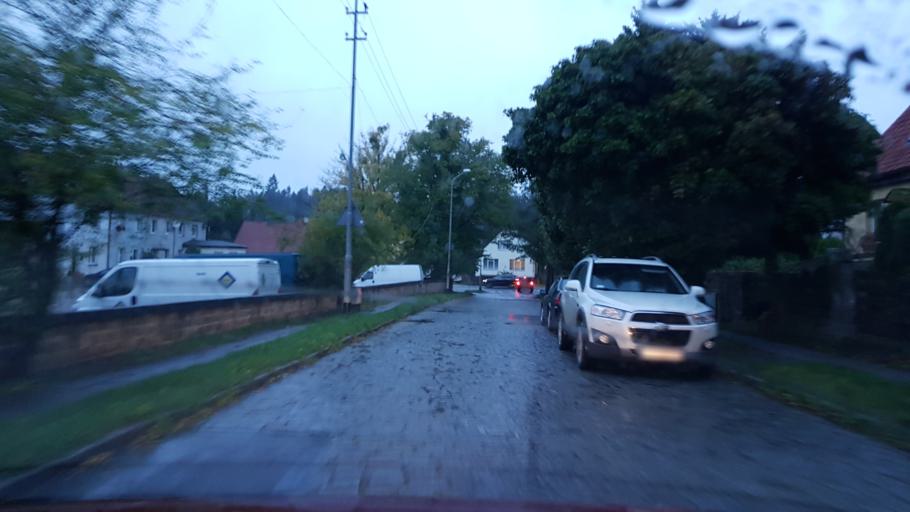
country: PL
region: West Pomeranian Voivodeship
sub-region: Powiat policki
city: Przeclaw
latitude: 53.4125
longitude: 14.5003
